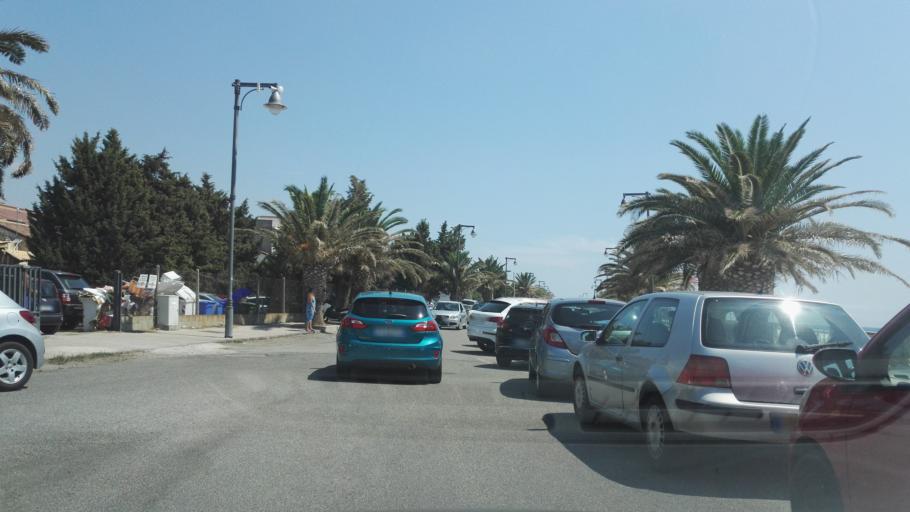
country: IT
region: Calabria
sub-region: Provincia di Reggio Calabria
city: Roccella Ionica
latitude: 38.3184
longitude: 16.3973
